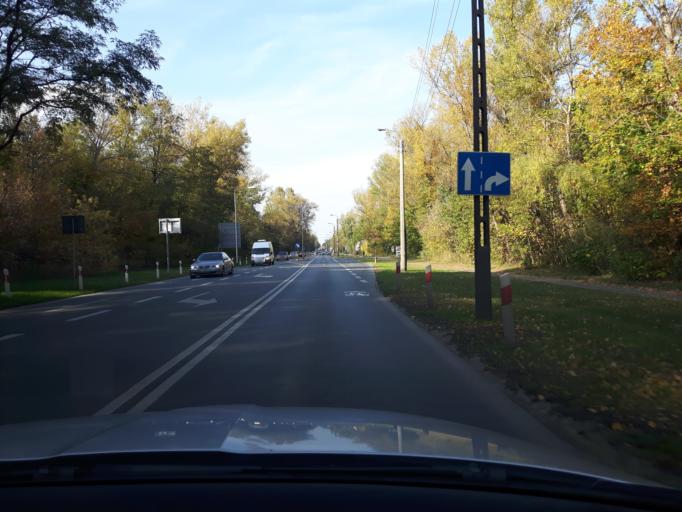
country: PL
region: Masovian Voivodeship
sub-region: Warszawa
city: Bialoleka
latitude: 52.3044
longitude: 21.0088
